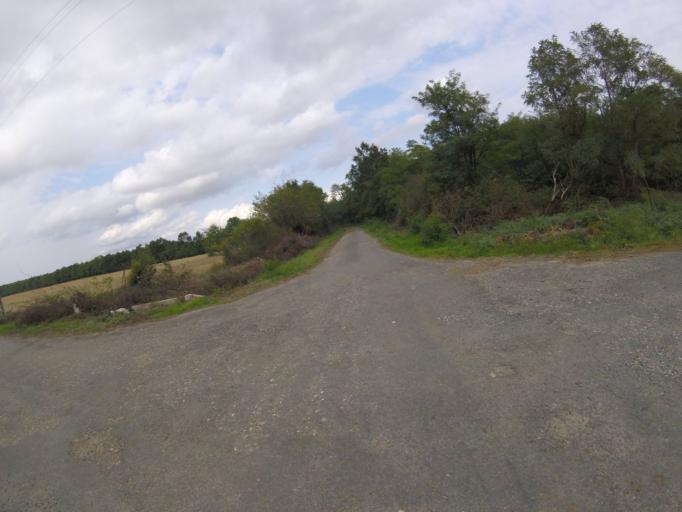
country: HU
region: Vas
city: Csepreg
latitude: 47.3716
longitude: 16.6747
